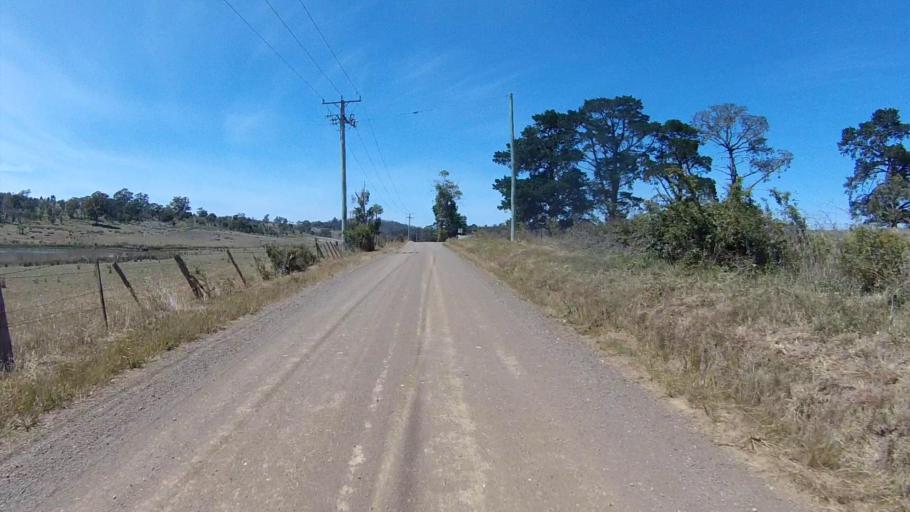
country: AU
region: Tasmania
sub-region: Sorell
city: Sorell
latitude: -42.7751
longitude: 147.6527
